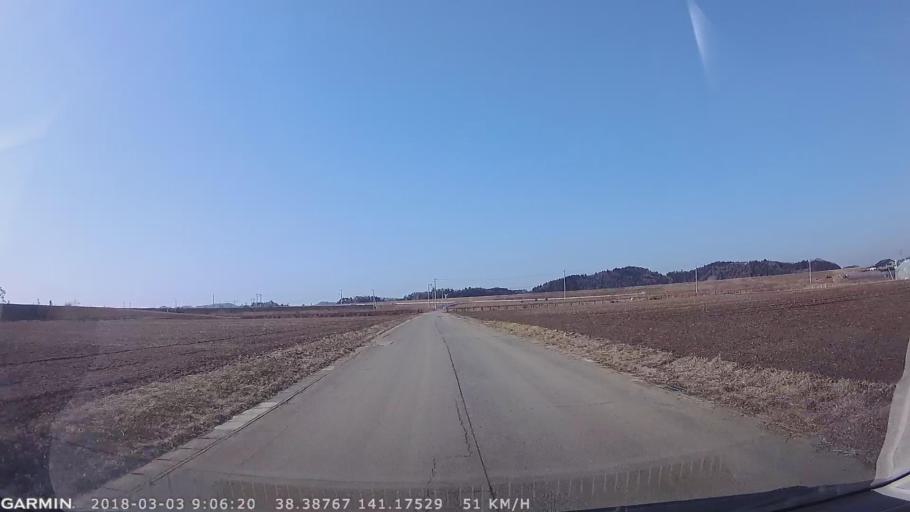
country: JP
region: Miyagi
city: Yamoto
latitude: 38.3877
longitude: 141.1753
